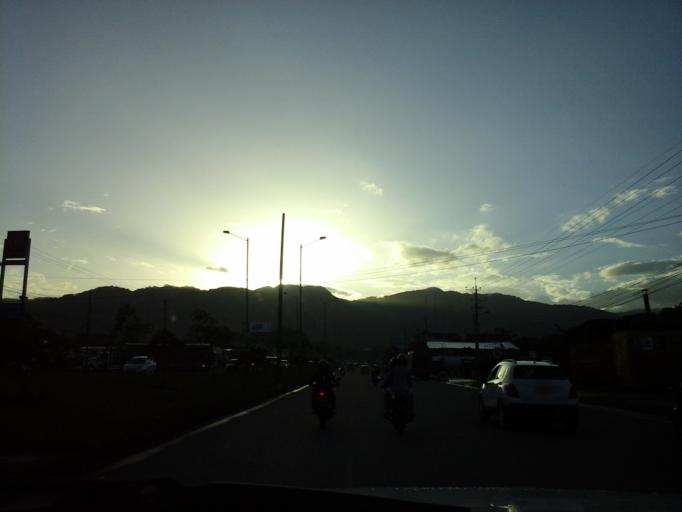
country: CO
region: Meta
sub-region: Villavicencio
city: Villavicencio
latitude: 4.1163
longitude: -73.6350
